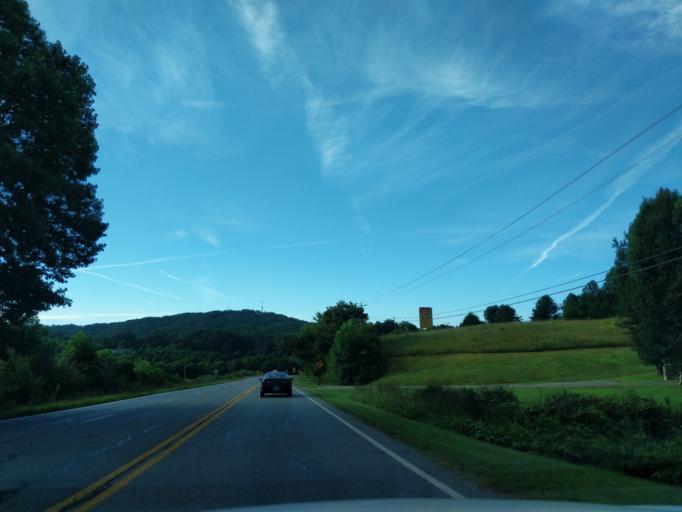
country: US
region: Georgia
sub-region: Fannin County
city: McCaysville
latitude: 34.9177
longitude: -84.3774
